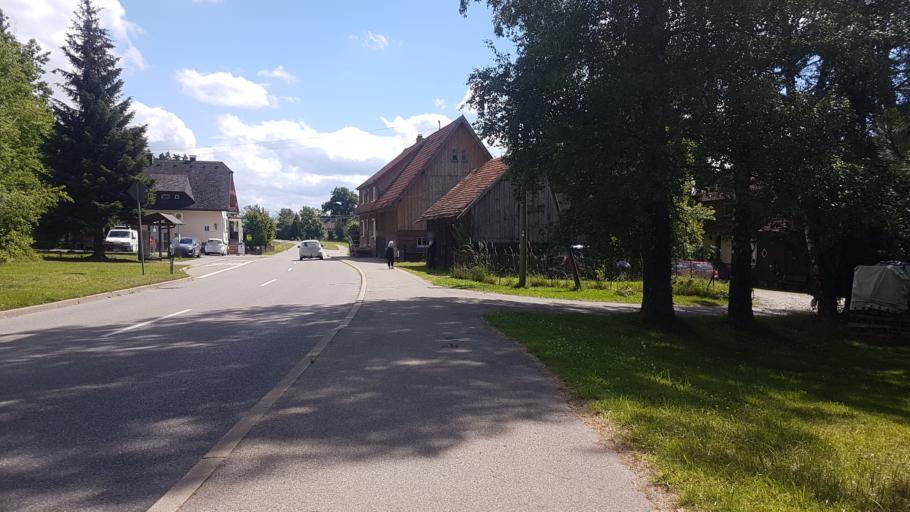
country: DE
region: Baden-Wuerttemberg
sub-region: Freiburg Region
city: Hardt
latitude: 48.2094
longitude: 8.4129
